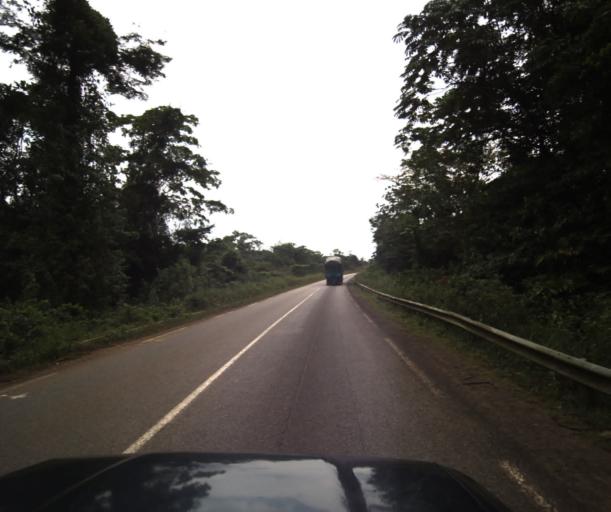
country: CM
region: Littoral
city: Edea
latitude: 3.8268
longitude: 10.3898
